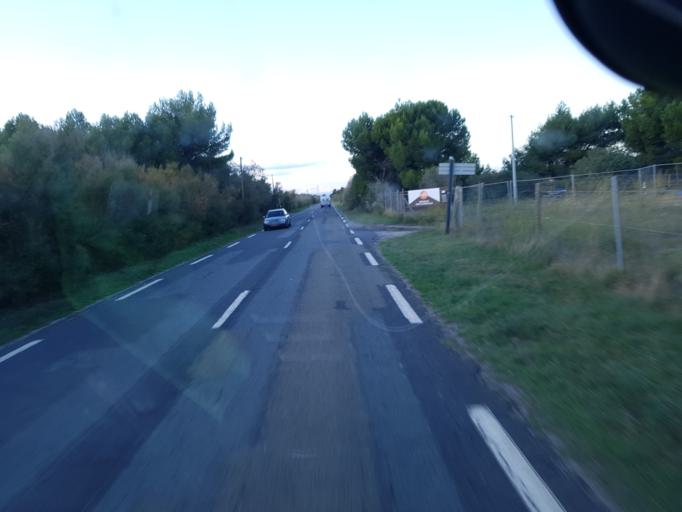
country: FR
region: Languedoc-Roussillon
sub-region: Departement de l'Aude
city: Port-la-Nouvelle
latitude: 43.0062
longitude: 3.0390
